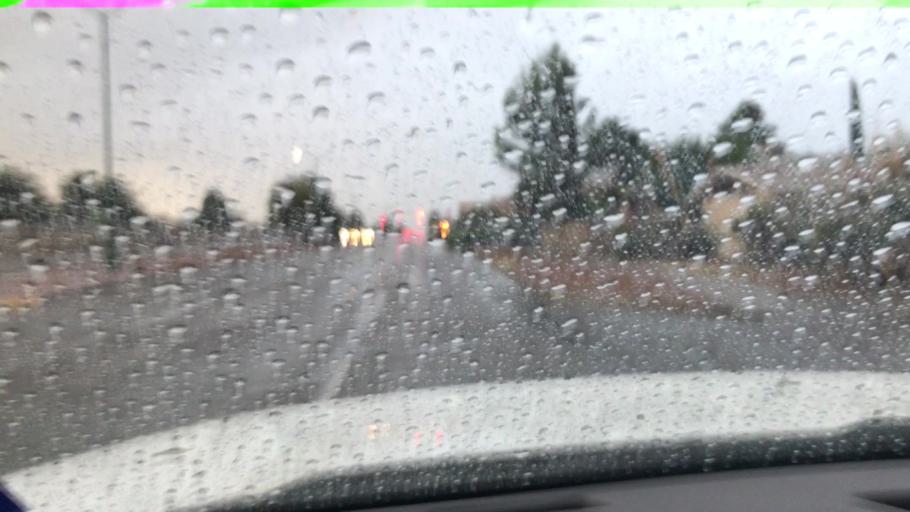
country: US
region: Texas
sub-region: El Paso County
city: Fort Bliss
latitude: 31.7936
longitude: -106.3234
